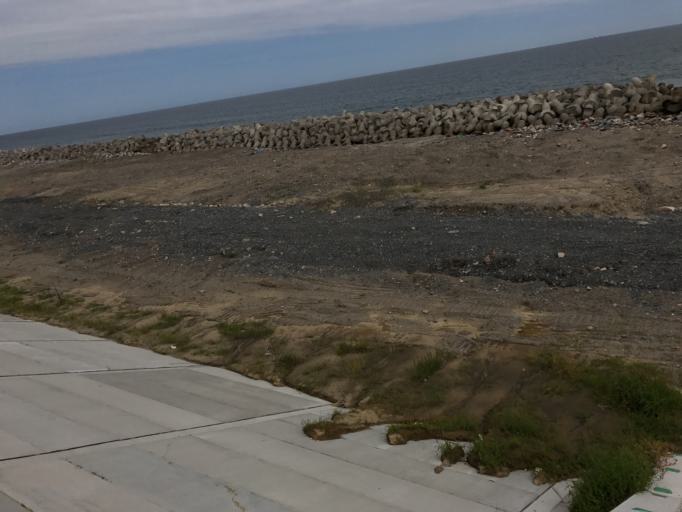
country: JP
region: Miyagi
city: Marumori
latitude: 37.7768
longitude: 140.9876
